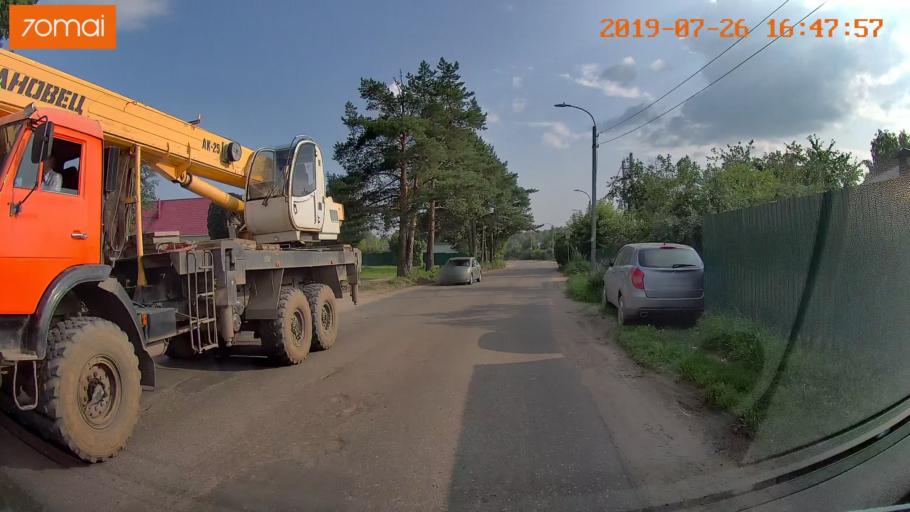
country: RU
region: Ivanovo
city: Bogorodskoye
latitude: 57.0380
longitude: 41.0126
